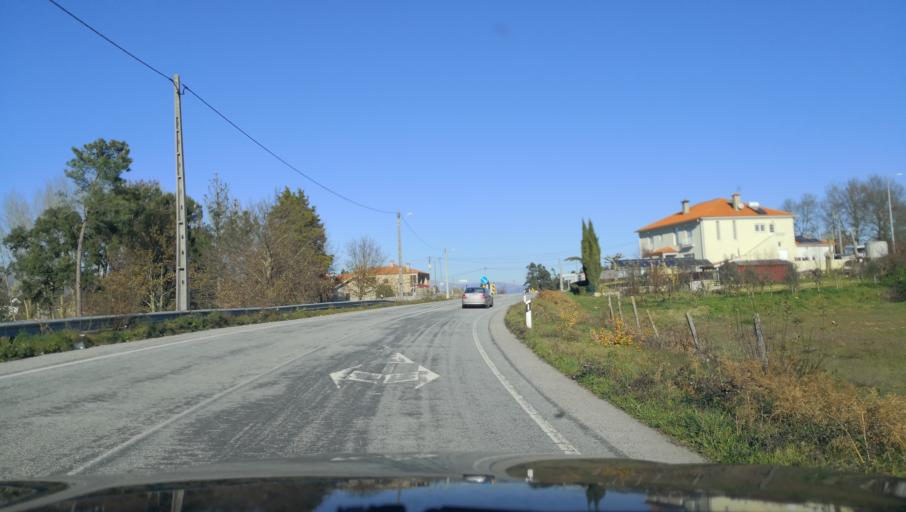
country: PT
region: Viseu
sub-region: Vouzela
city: Vouzela
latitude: 40.7160
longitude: -8.1353
